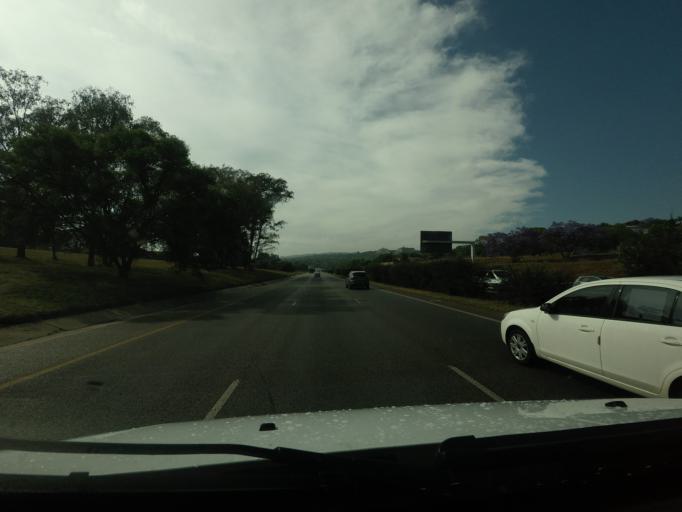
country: ZA
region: Gauteng
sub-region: City of Tshwane Metropolitan Municipality
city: Pretoria
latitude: -25.7460
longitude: 28.2924
